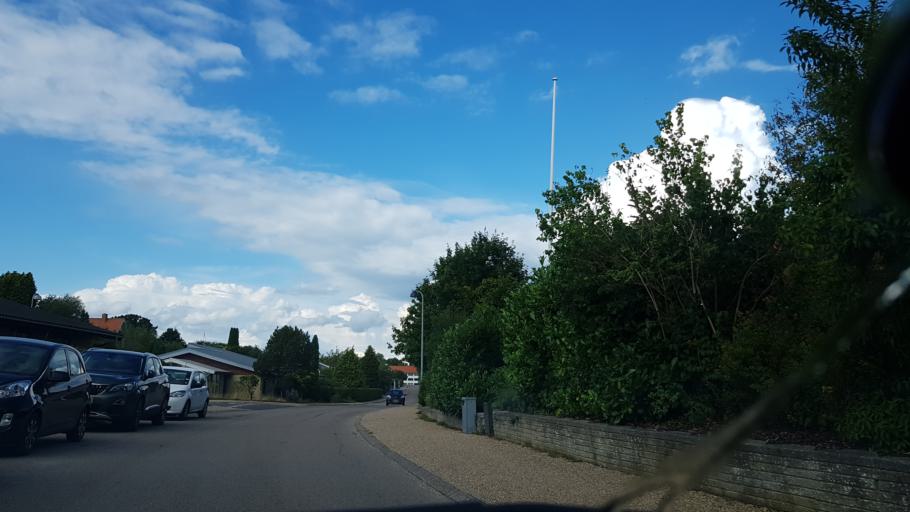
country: DK
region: Capital Region
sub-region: Fredensborg Kommune
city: Humlebaek
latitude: 55.9900
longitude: 12.5382
